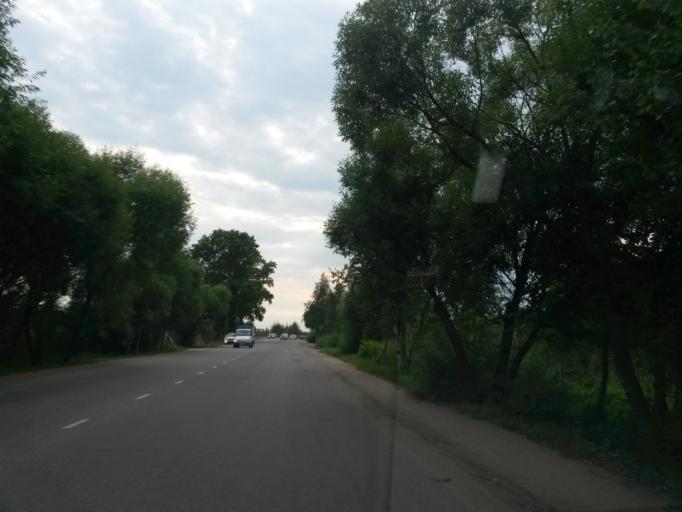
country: RU
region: Jaroslavl
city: Yaroslavl
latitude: 57.6037
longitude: 39.7994
